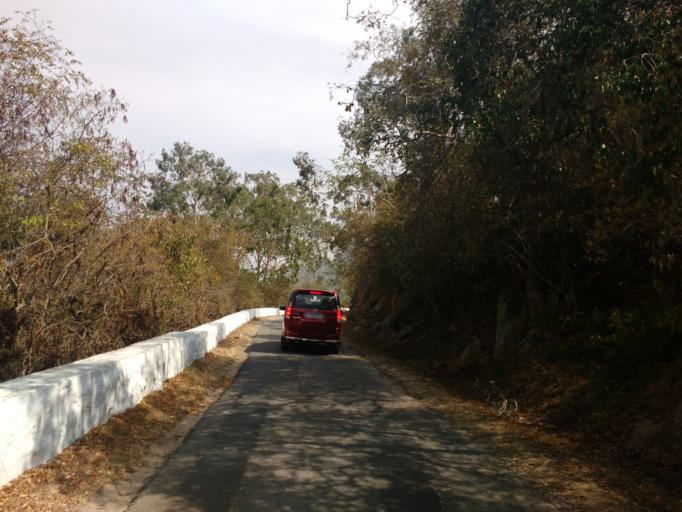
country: IN
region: Karnataka
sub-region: Mysore
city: Mysore
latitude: 12.2815
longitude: 76.6702
